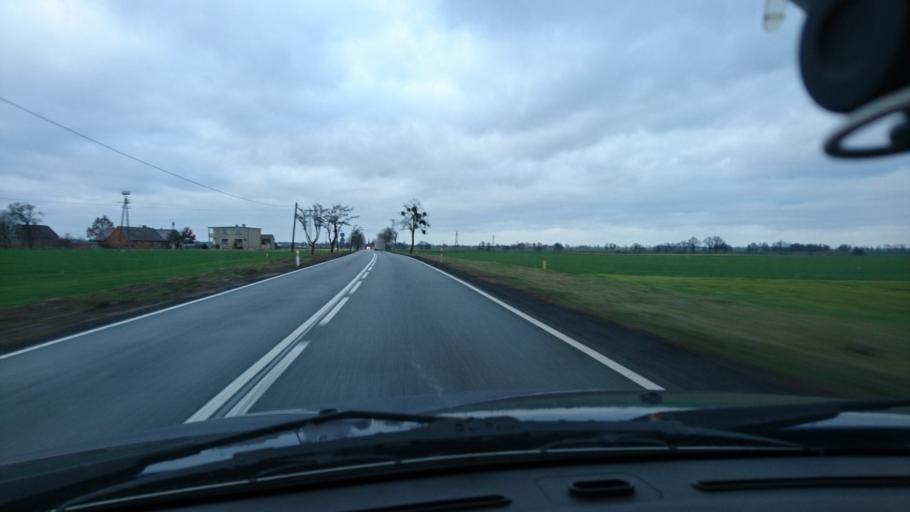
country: PL
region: Opole Voivodeship
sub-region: Powiat kluczborski
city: Kluczbork
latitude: 51.0104
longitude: 18.2038
